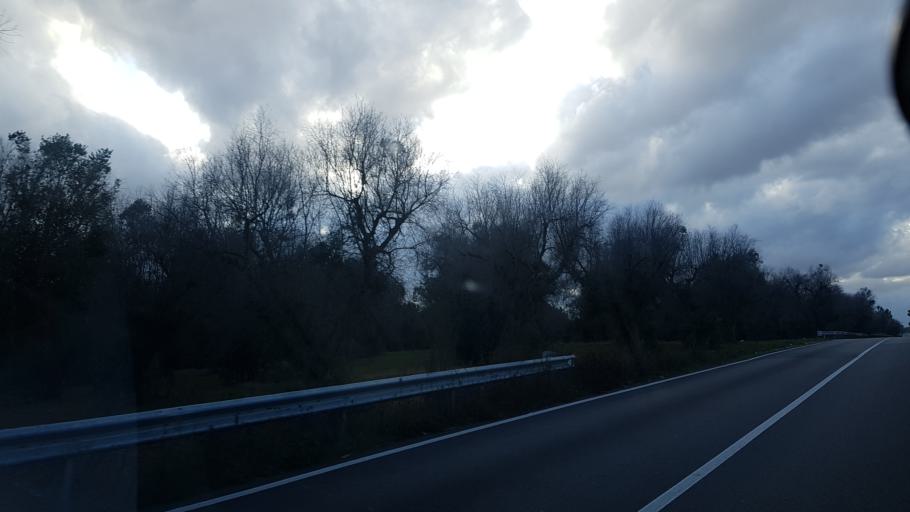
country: IT
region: Apulia
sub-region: Provincia di Brindisi
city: Torchiarolo
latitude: 40.4870
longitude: 18.0341
